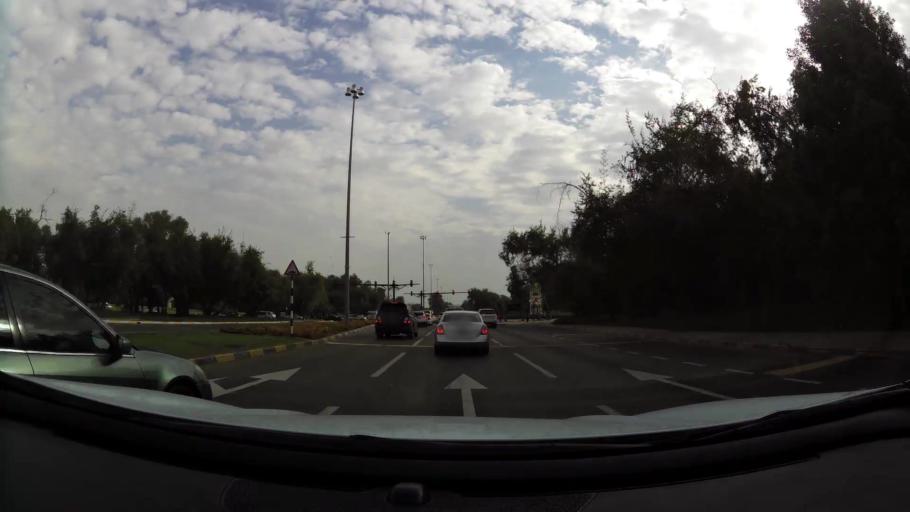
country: AE
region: Abu Dhabi
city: Al Ain
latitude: 24.1864
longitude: 55.6361
